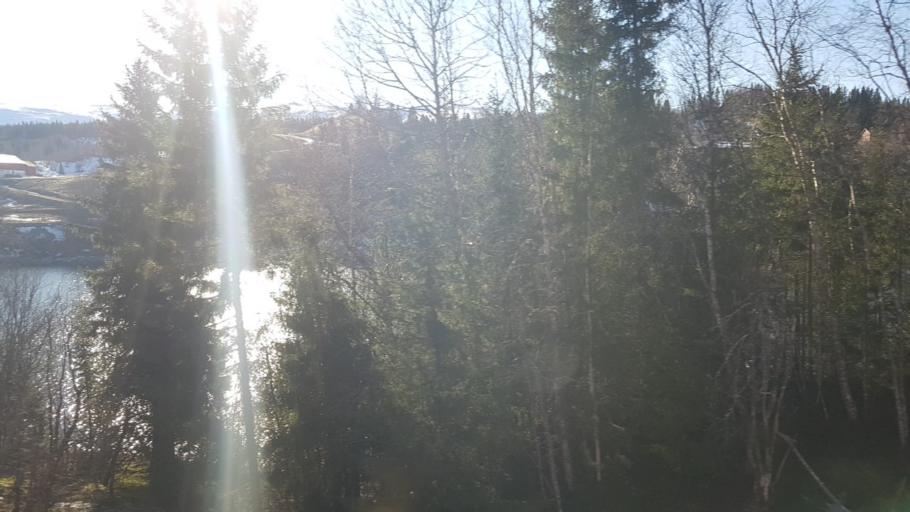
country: NO
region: Nordland
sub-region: Vefsn
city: Mosjoen
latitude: 65.7869
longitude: 13.2447
